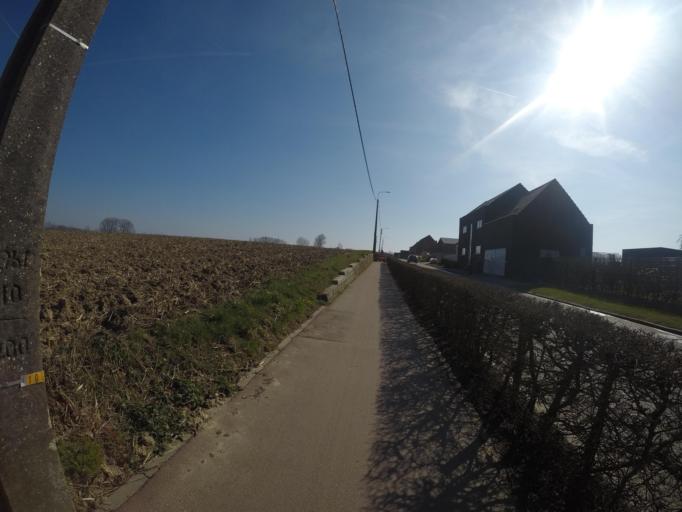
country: BE
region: Flanders
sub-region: Provincie Oost-Vlaanderen
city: Sint-Maria-Lierde
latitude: 50.7944
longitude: 3.8308
